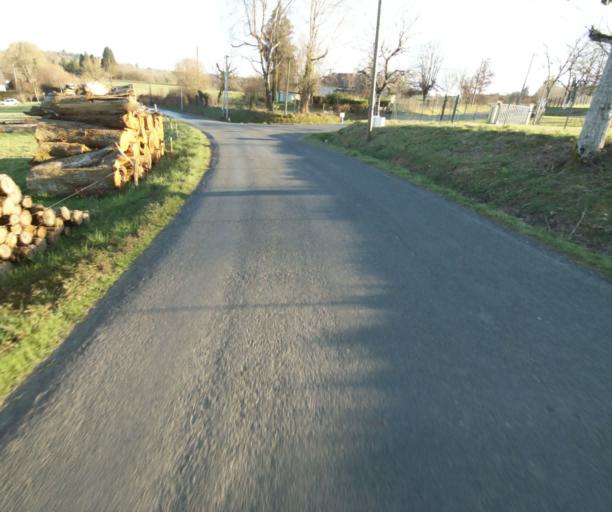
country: FR
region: Limousin
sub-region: Departement de la Correze
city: Saint-Clement
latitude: 45.3454
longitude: 1.6646
